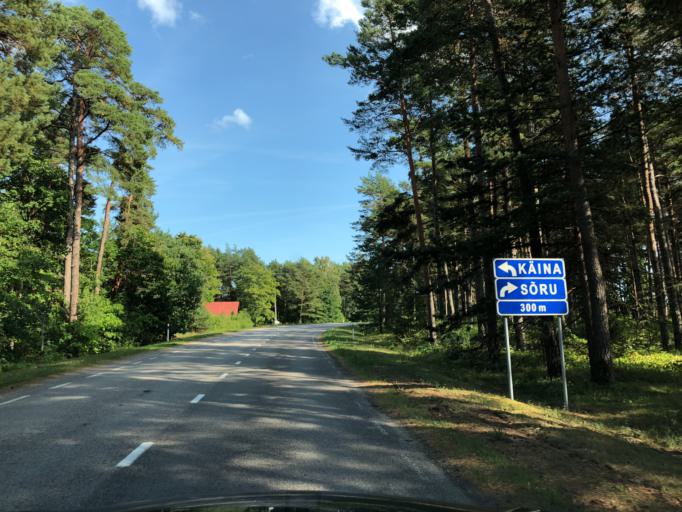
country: EE
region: Hiiumaa
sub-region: Kaerdla linn
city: Kardla
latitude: 58.7072
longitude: 22.5930
